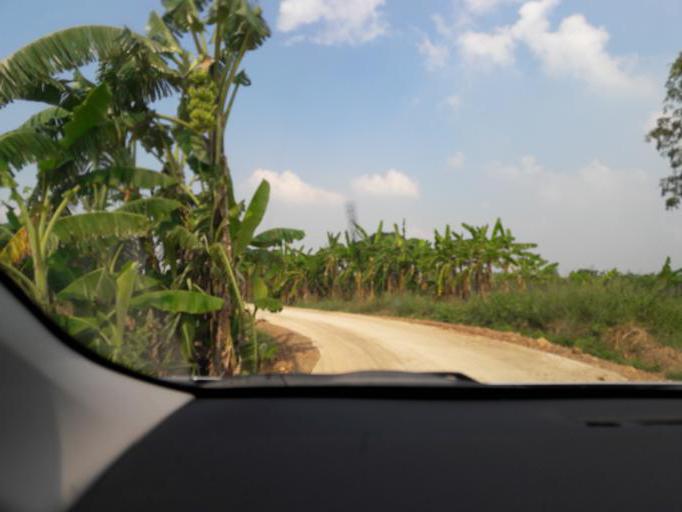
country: TH
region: Ang Thong
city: Ang Thong
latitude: 14.5616
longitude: 100.4176
